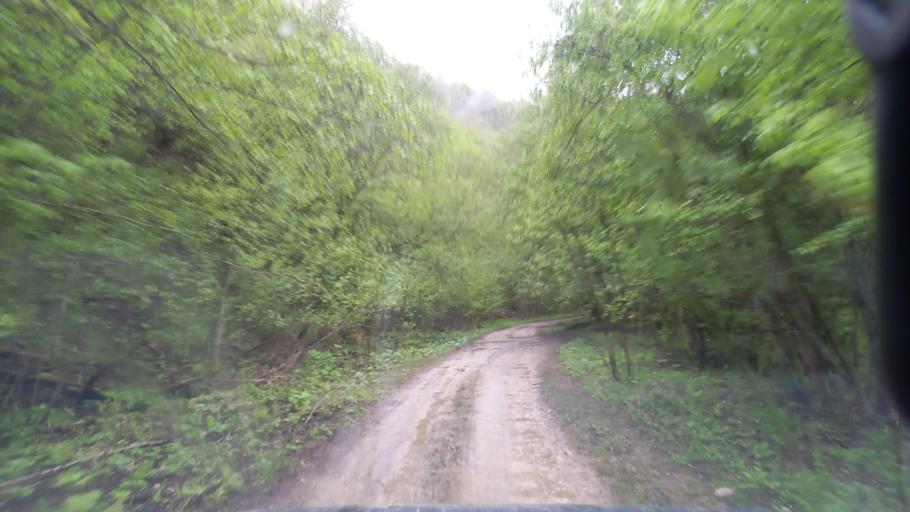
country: RU
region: Kabardino-Balkariya
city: Bylym
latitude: 43.5904
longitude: 42.9738
